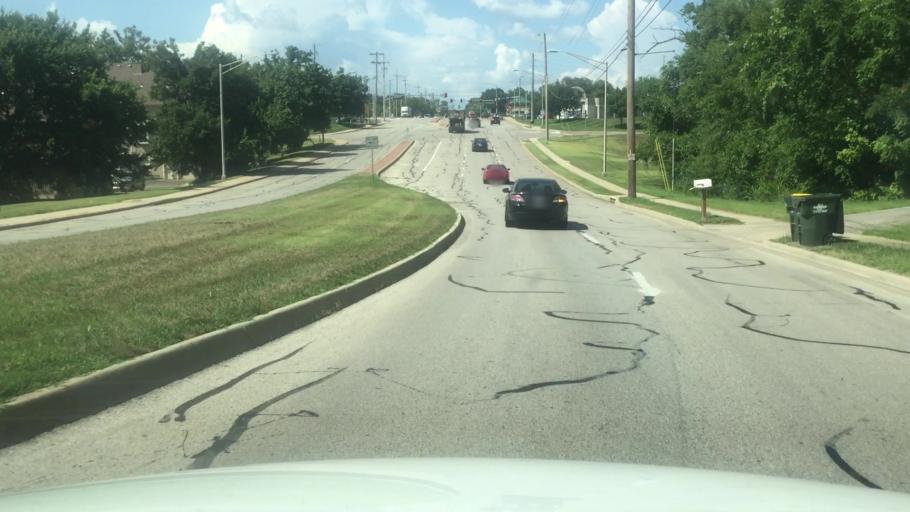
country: US
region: Kansas
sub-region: Johnson County
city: Shawnee
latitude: 39.0113
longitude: -94.7424
